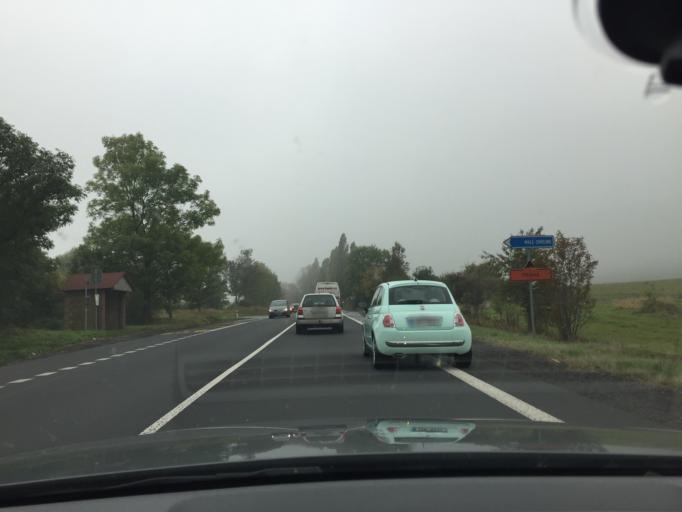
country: CZ
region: Ustecky
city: Libouchec
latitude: 50.7446
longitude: 14.0227
